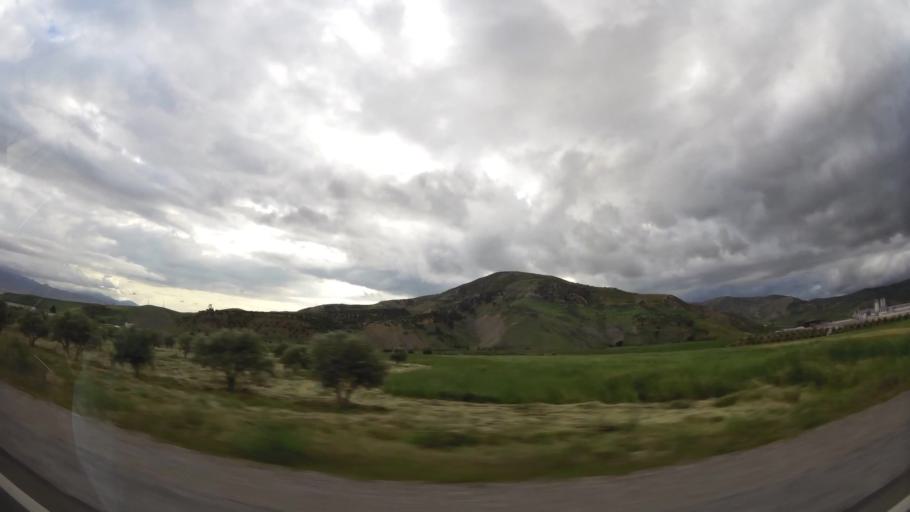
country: MA
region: Taza-Al Hoceima-Taounate
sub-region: Taza
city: Taza
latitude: 34.2762
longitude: -3.9562
